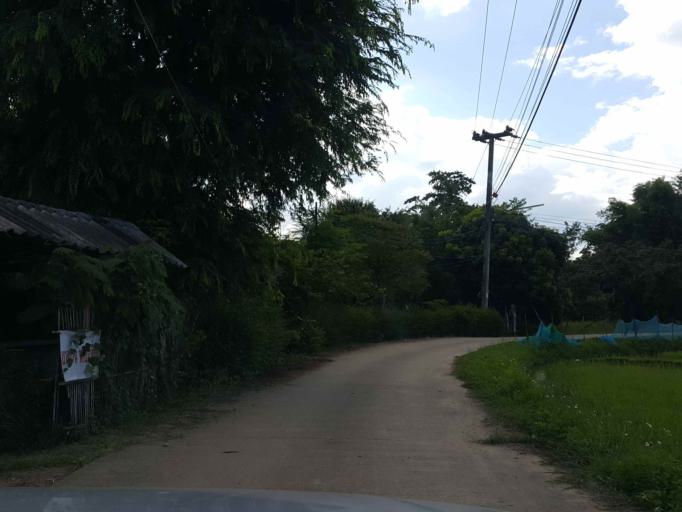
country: TH
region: Chiang Mai
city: Mae Taeng
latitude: 18.9669
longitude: 98.9174
